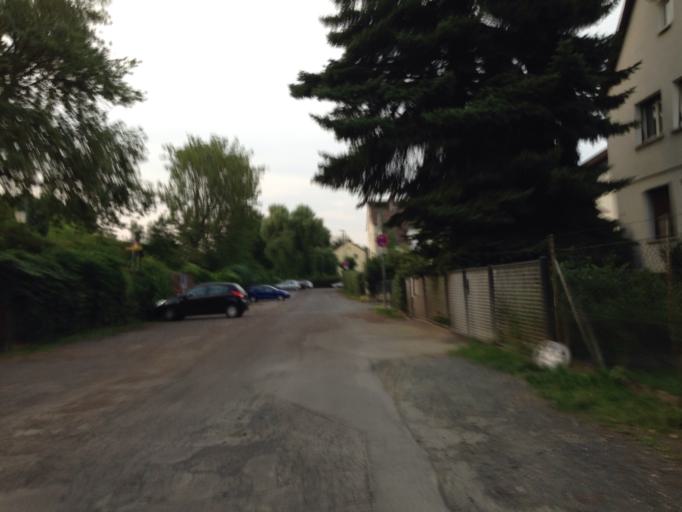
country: DE
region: Hesse
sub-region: Regierungsbezirk Giessen
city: Giessen
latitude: 50.5916
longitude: 8.6716
